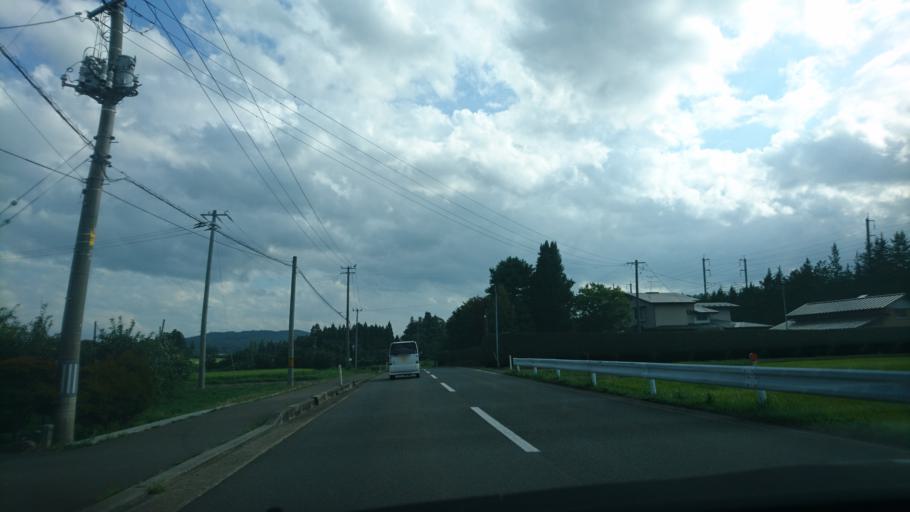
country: JP
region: Iwate
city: Hanamaki
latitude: 39.4270
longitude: 141.1786
